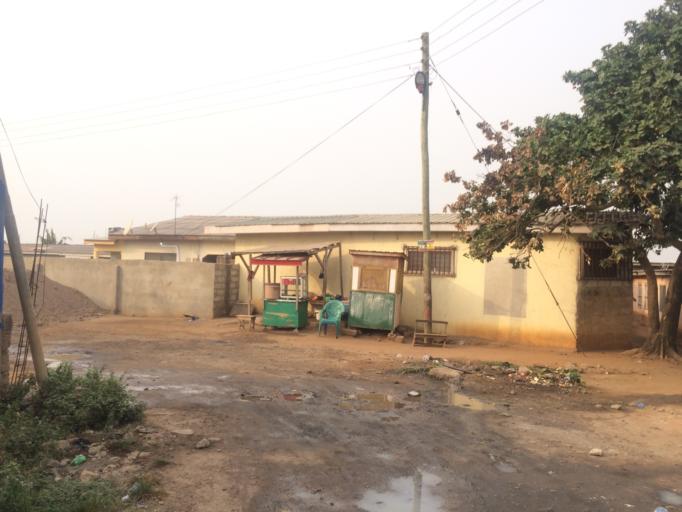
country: GH
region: Greater Accra
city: Nungua
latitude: 5.6043
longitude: -0.0859
